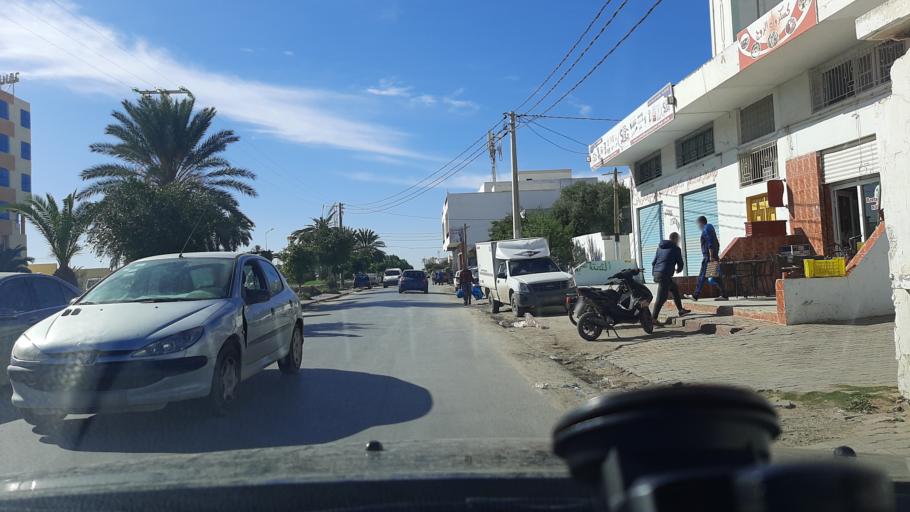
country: TN
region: Safaqis
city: Sfax
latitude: 34.7220
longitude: 10.7344
